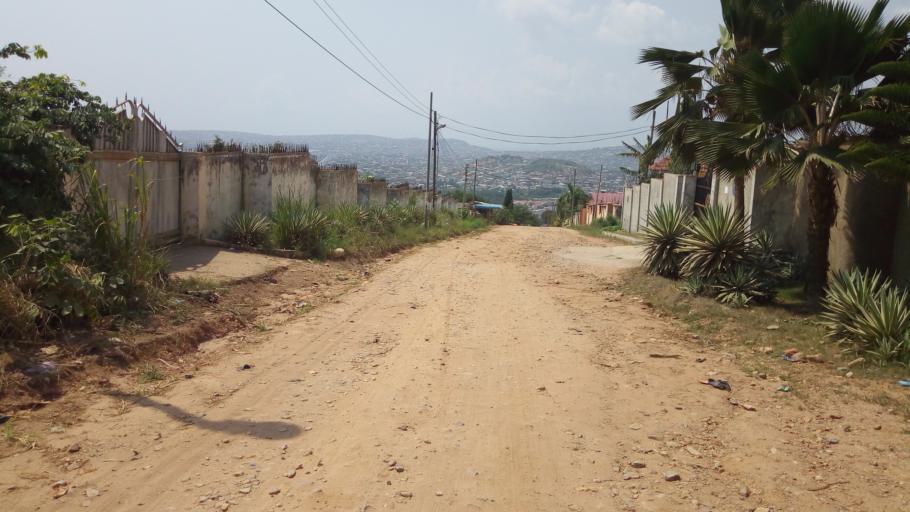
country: GH
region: Greater Accra
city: Gbawe
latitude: 5.5629
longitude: -0.3037
